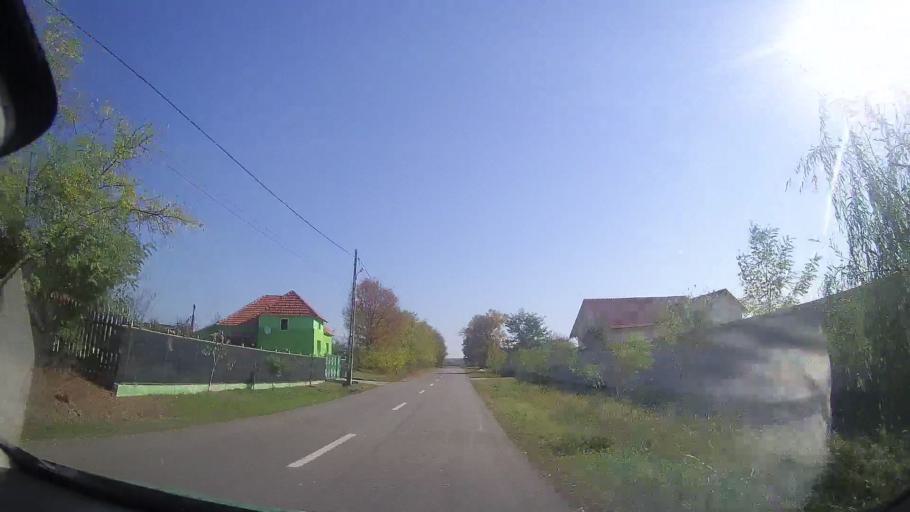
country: RO
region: Timis
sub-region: Comuna Secas
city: Secas
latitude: 45.8446
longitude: 21.7860
